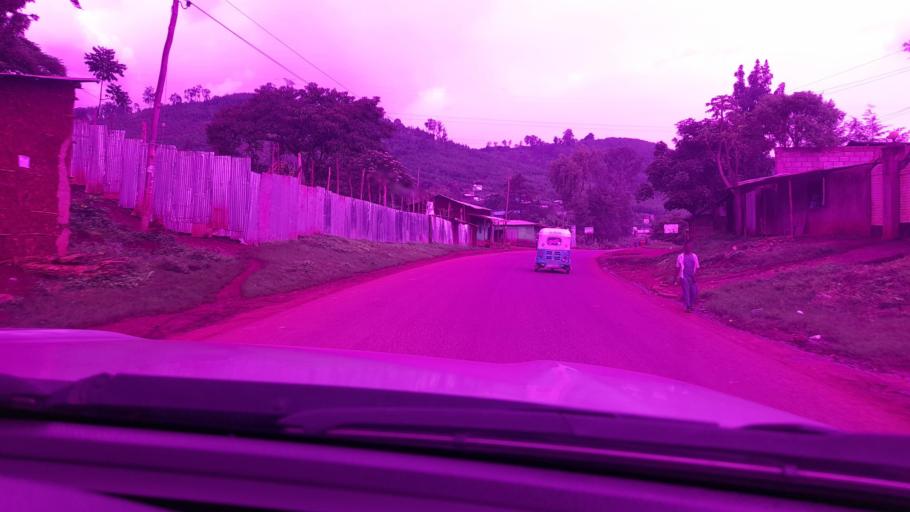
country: ET
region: Oromiya
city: Jima
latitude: 7.6699
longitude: 36.8666
